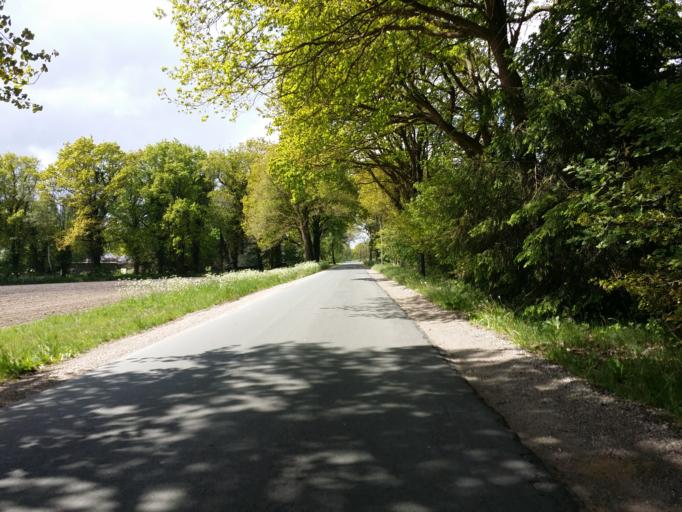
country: DE
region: Lower Saxony
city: Kirchseelte
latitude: 52.9831
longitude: 8.6668
